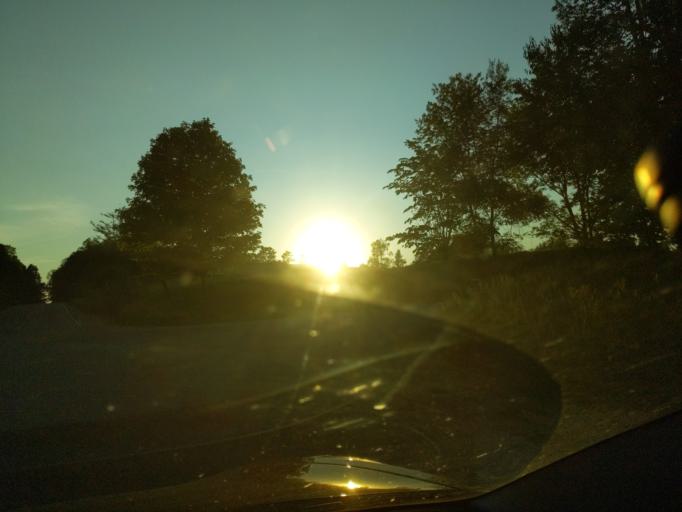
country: US
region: Michigan
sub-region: Barry County
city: Nashville
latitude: 42.5381
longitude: -85.1131
